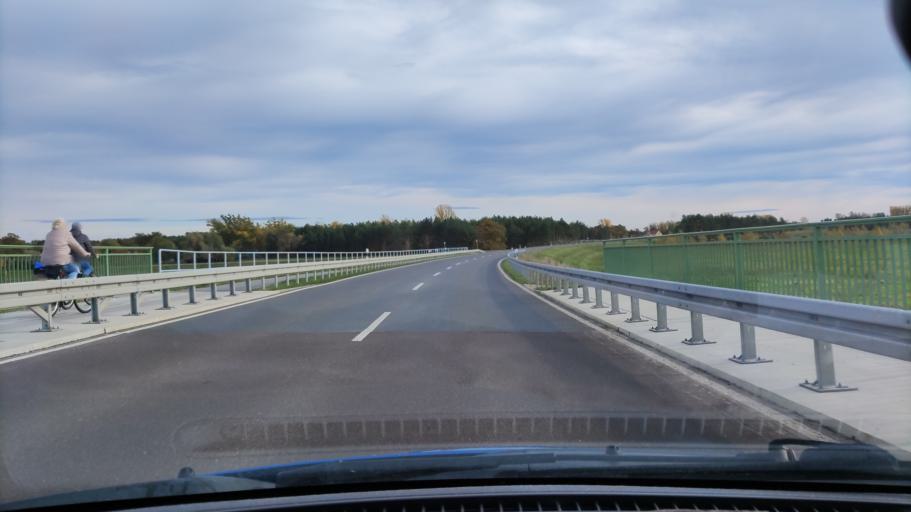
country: DE
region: Brandenburg
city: Wittenberge
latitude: 53.0081
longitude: 11.7739
